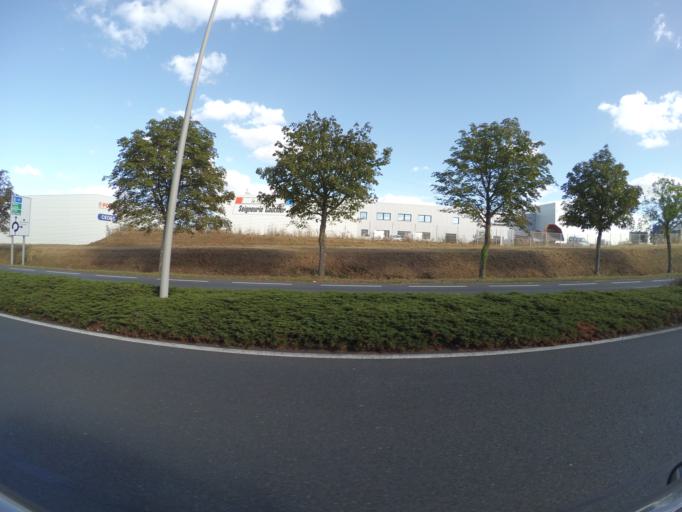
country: FR
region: Pays de la Loire
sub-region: Departement de Maine-et-Loire
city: Mazieres-en-Mauges
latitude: 47.0688
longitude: -0.8420
